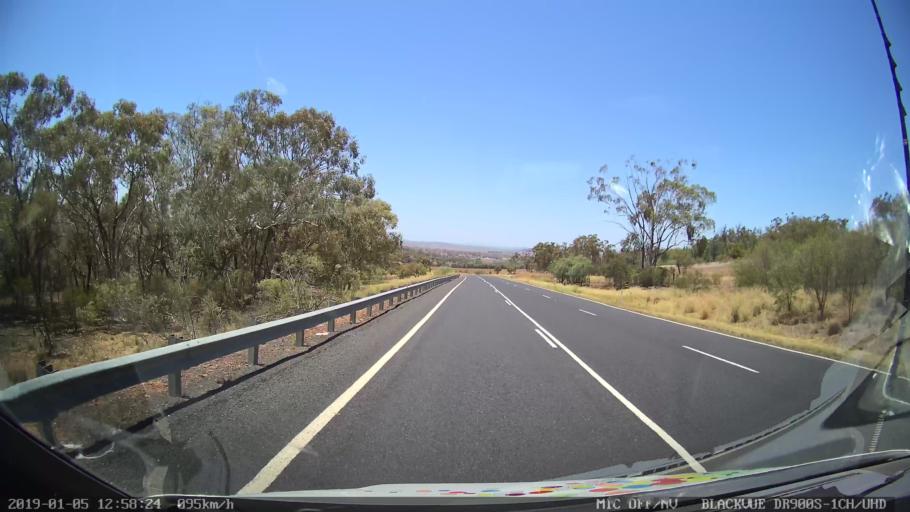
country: AU
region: New South Wales
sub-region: Narrabri
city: Boggabri
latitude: -31.1126
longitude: 149.7492
